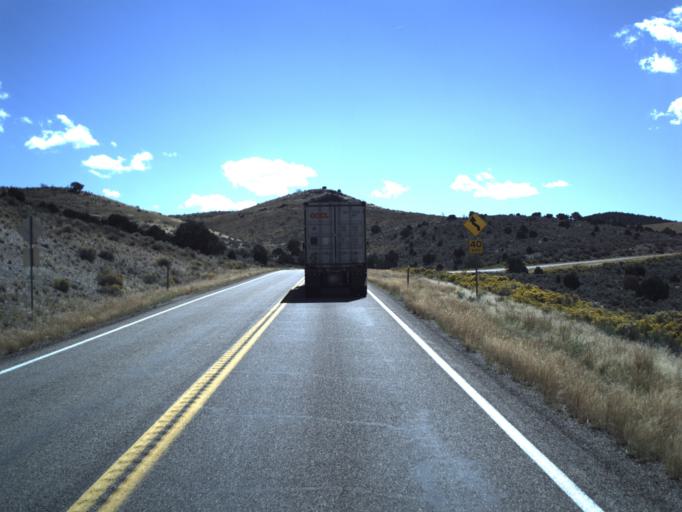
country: US
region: Utah
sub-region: Beaver County
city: Milford
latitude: 38.1103
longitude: -112.9476
